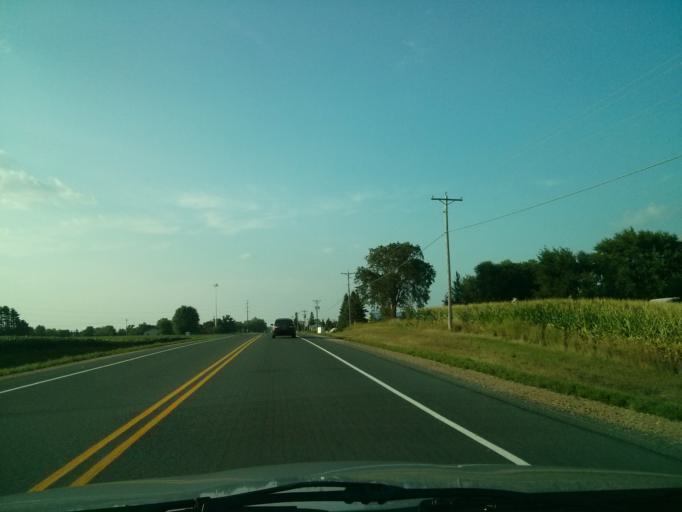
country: US
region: Wisconsin
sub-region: Saint Croix County
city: North Hudson
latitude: 45.0004
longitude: -92.6754
